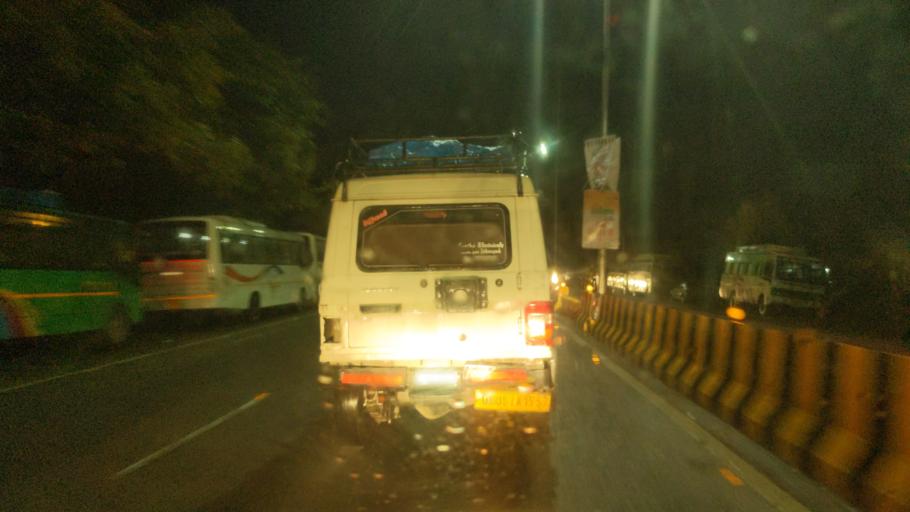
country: IN
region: Uttarakhand
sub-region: Naini Tal
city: Haldwani
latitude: 29.2587
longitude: 79.5431
